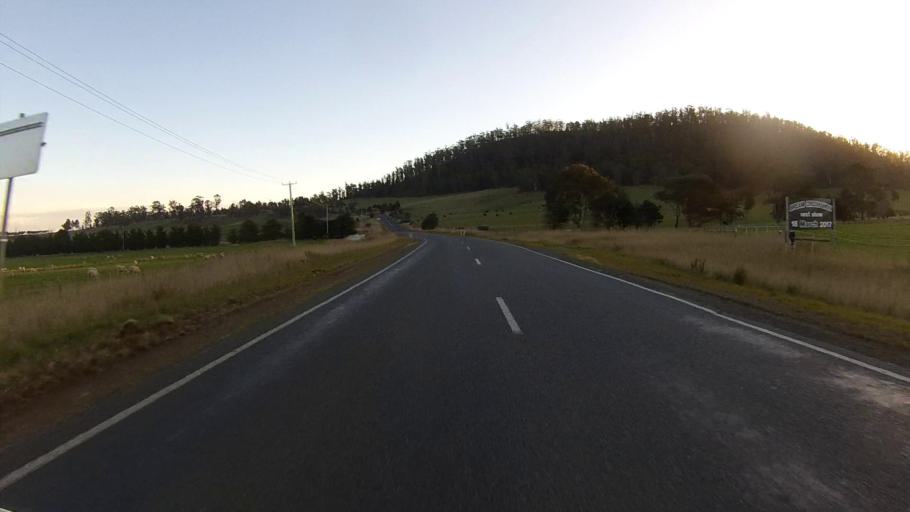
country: AU
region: Tasmania
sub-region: Sorell
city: Sorell
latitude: -42.8187
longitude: 147.7490
